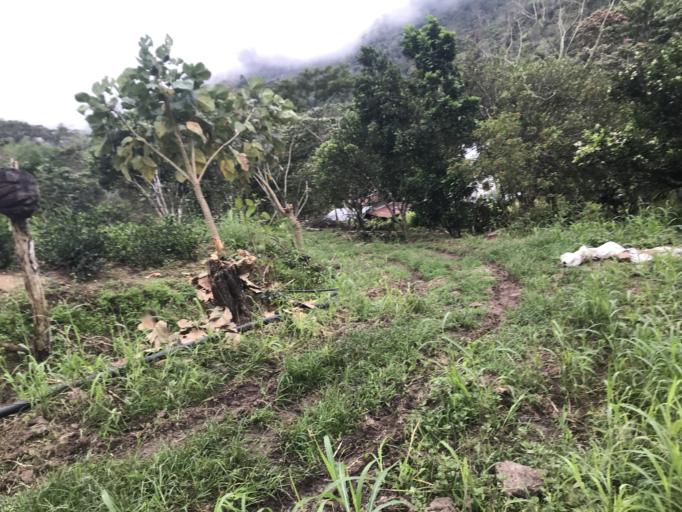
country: PE
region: Pasco
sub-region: Provincia de Oxapampa
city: Villa Rica
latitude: -10.8312
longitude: -75.2925
